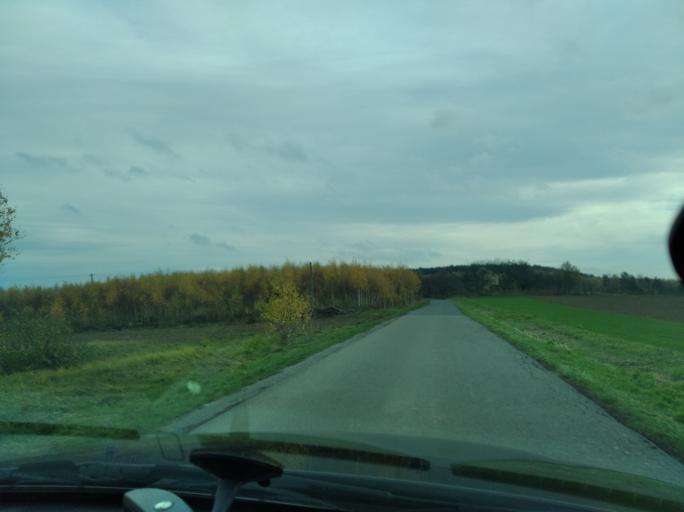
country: PL
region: Subcarpathian Voivodeship
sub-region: Powiat strzyzowski
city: Strzyzow
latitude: 49.9166
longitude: 21.7652
